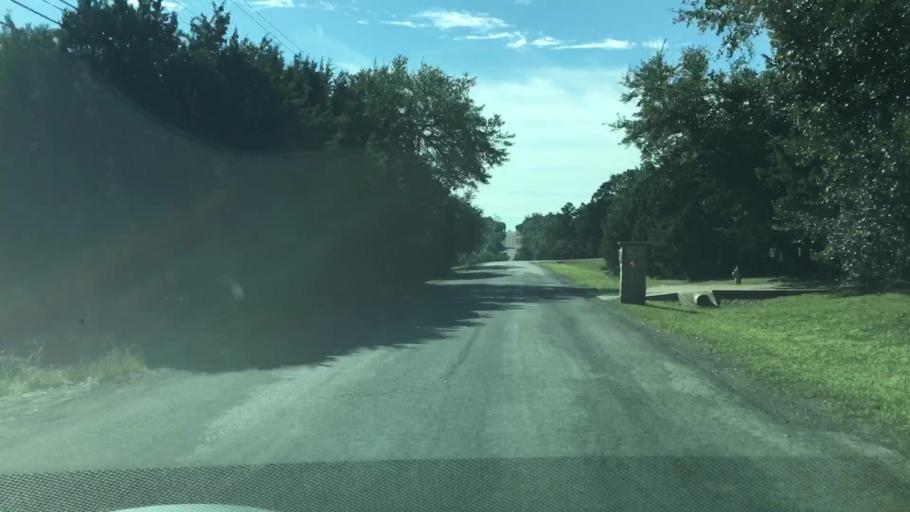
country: US
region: Texas
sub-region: Hays County
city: Dripping Springs
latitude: 30.1957
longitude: -98.0195
